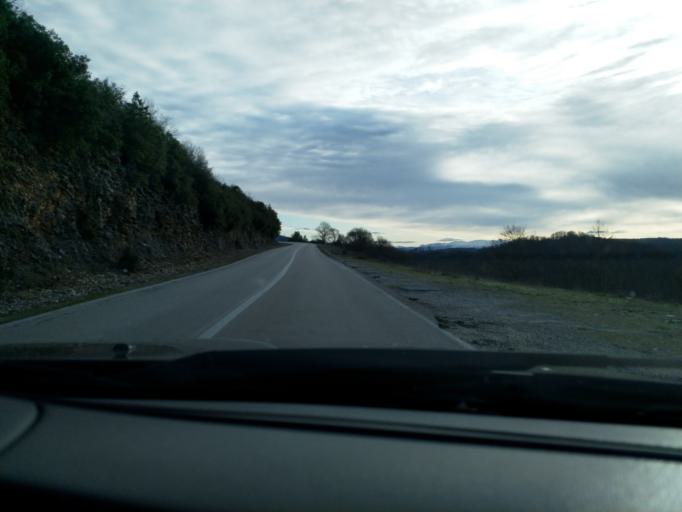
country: GR
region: Epirus
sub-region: Nomos Ioanninon
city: Asprangeloi
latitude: 39.8689
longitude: 20.7381
